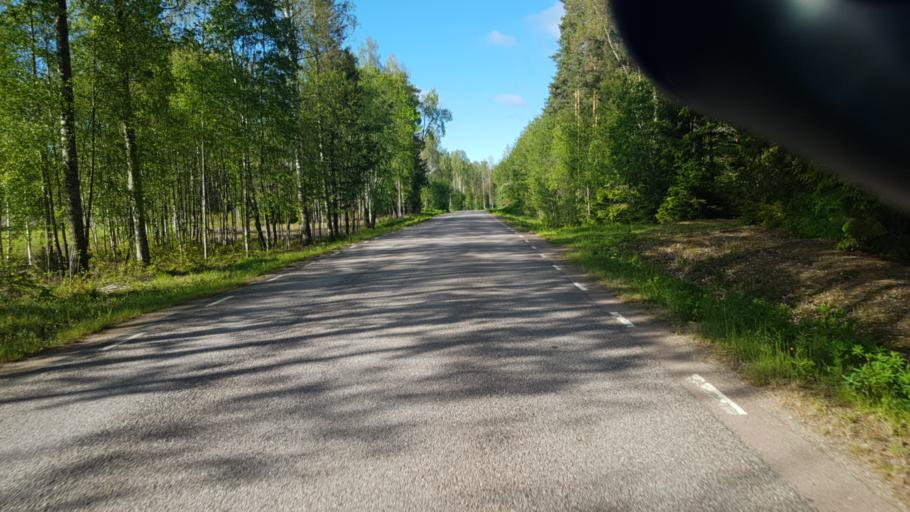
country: SE
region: Vaermland
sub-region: Arvika Kommun
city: Arvika
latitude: 59.5802
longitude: 12.7238
